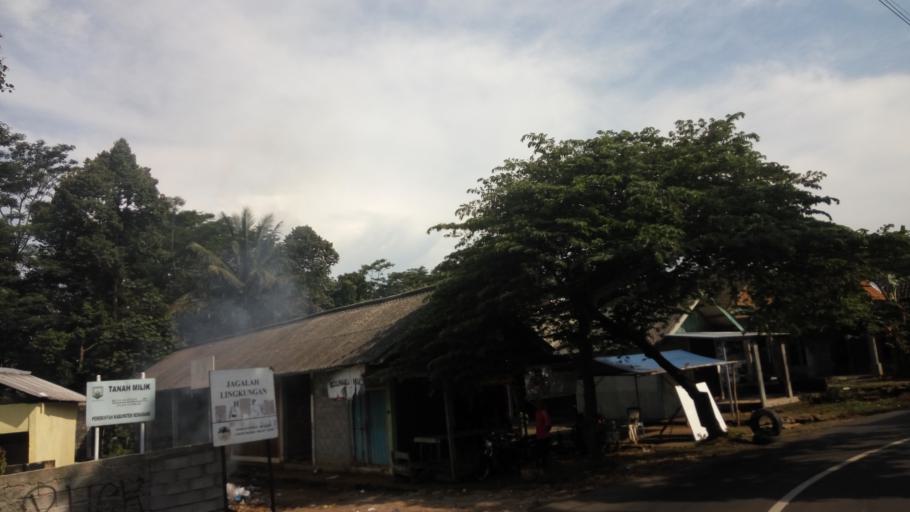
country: ID
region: Central Java
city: Ungaran
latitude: -7.1447
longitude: 110.4217
